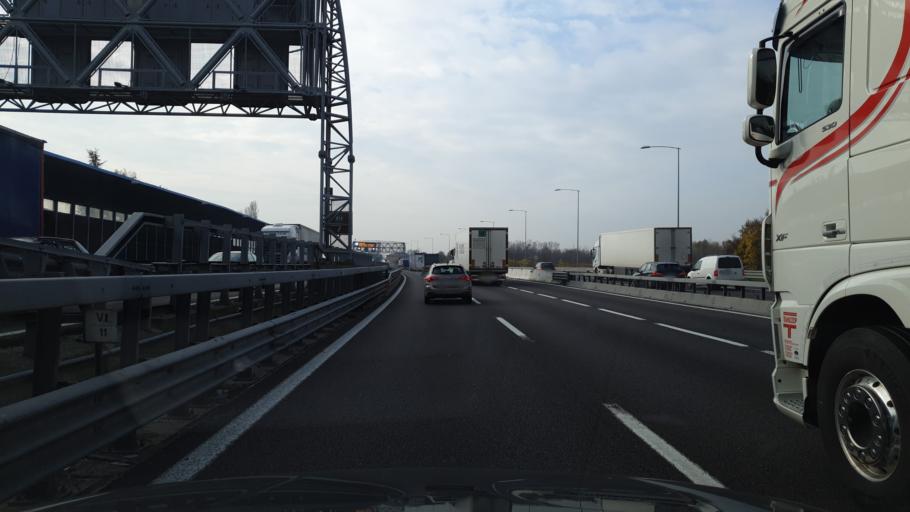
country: IT
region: Emilia-Romagna
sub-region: Provincia di Bologna
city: Trebbo
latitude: 44.5320
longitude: 11.3236
